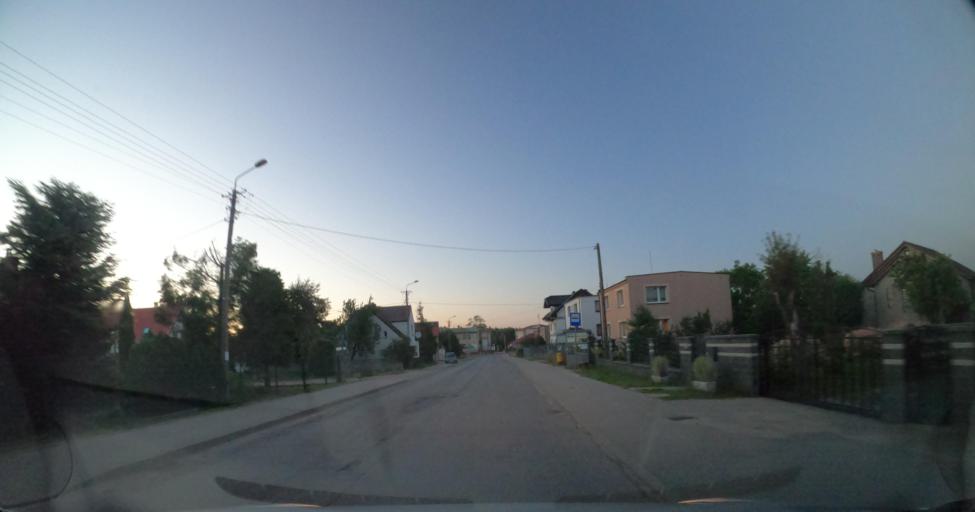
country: PL
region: Pomeranian Voivodeship
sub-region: Powiat wejherowski
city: Szemud
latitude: 54.4857
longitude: 18.2193
